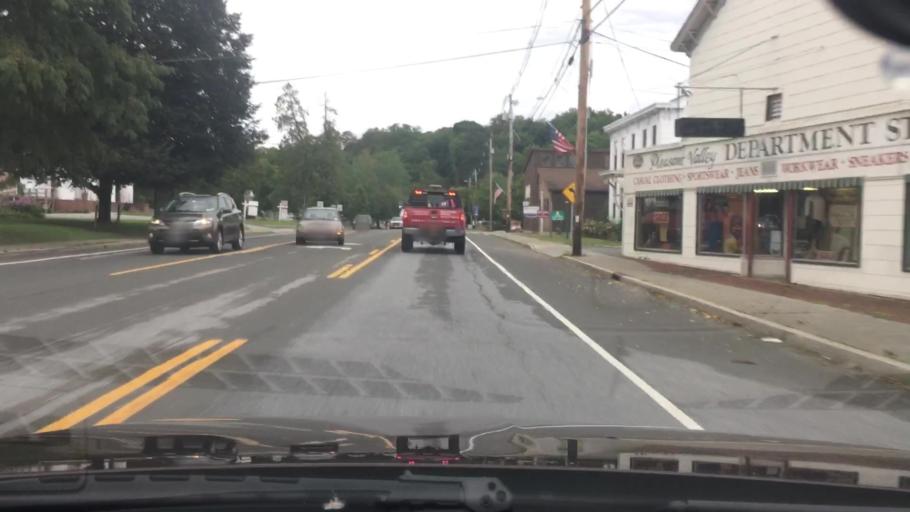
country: US
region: New York
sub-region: Dutchess County
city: Pleasant Valley
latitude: 41.7441
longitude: -73.8256
